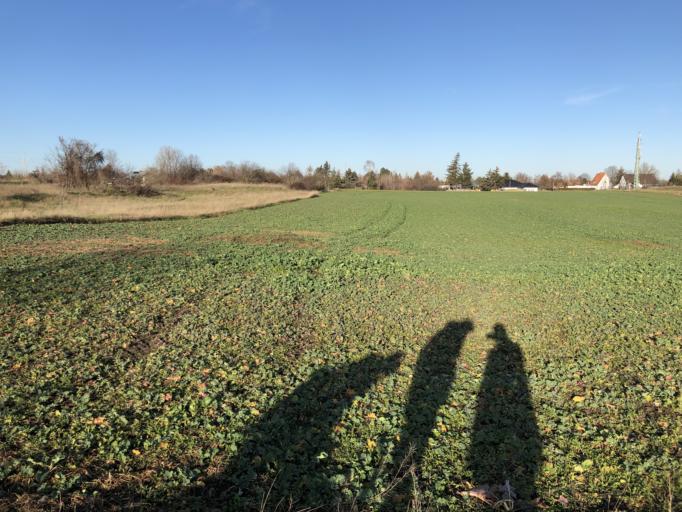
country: DE
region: Saxony-Anhalt
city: Halle (Saale)
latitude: 51.4915
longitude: 12.0218
